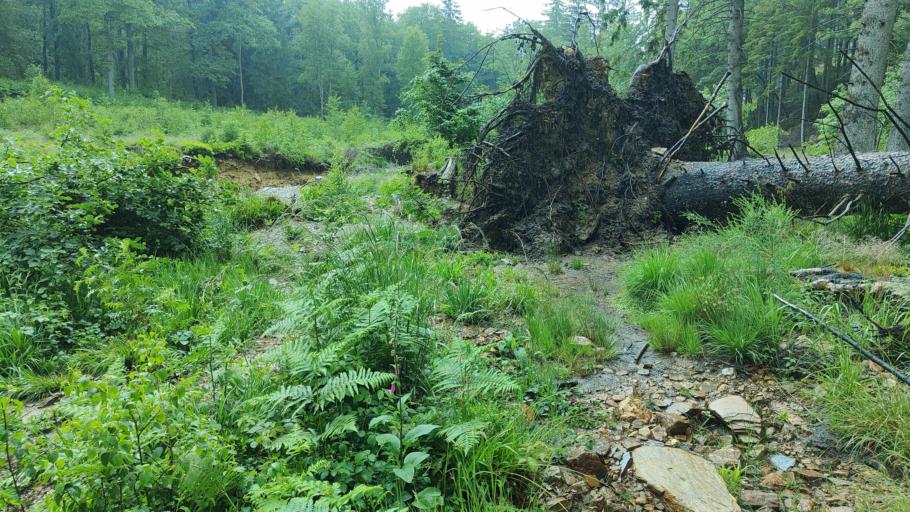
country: DE
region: North Rhine-Westphalia
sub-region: Regierungsbezirk Koln
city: Roetgen
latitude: 50.6233
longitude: 6.1636
